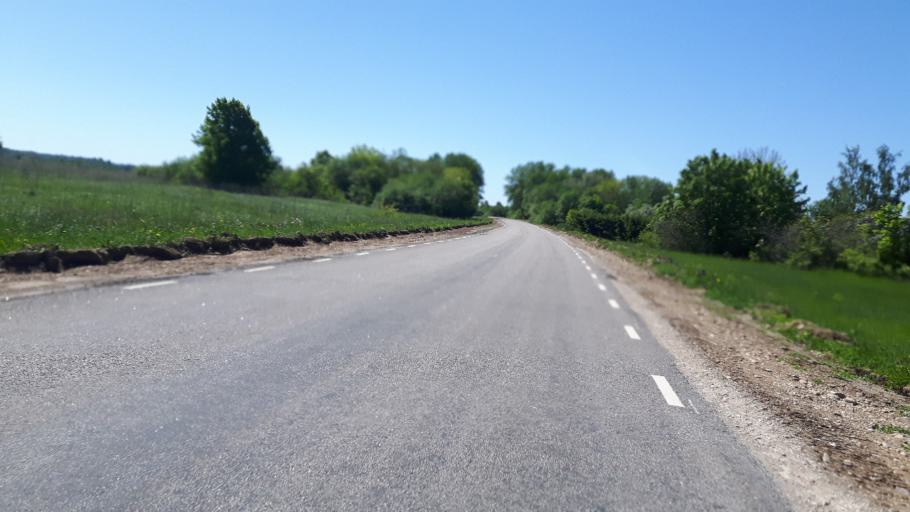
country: EE
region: Ida-Virumaa
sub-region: Narva-Joesuu linn
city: Narva-Joesuu
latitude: 59.3937
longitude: 27.9245
